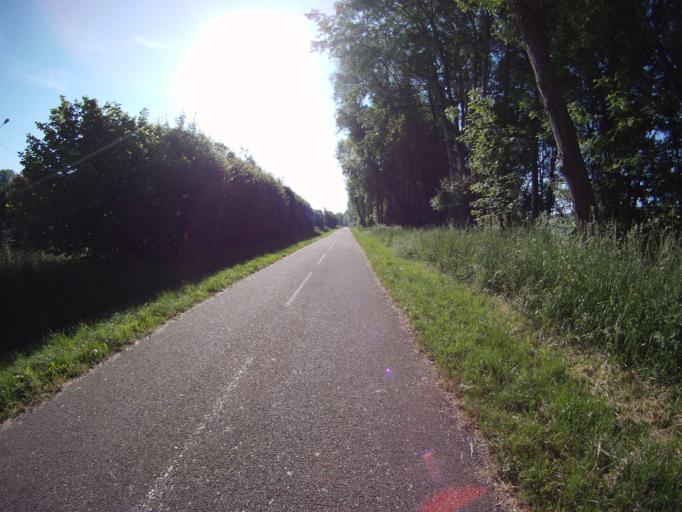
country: FR
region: Lorraine
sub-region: Departement de Meurthe-et-Moselle
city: Lay-Saint-Christophe
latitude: 48.7451
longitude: 6.2087
